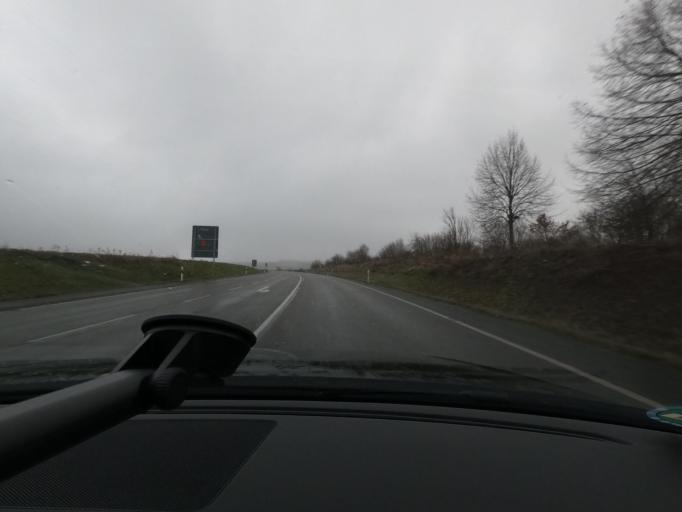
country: DE
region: Thuringia
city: Silberhausen
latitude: 51.3055
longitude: 10.3283
